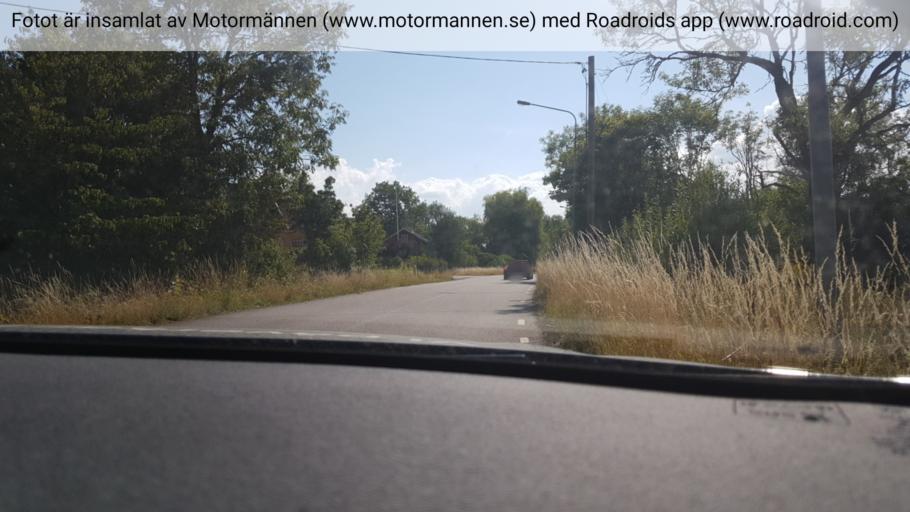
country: SE
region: Vaestra Goetaland
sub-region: Gotene Kommun
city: Kallby
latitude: 58.5588
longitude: 13.3496
